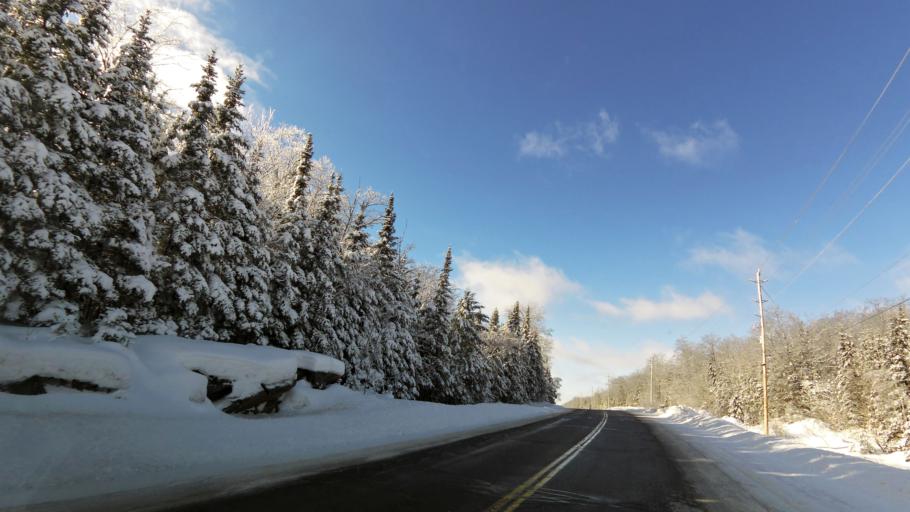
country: CA
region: Ontario
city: Bancroft
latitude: 45.0114
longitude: -78.3183
